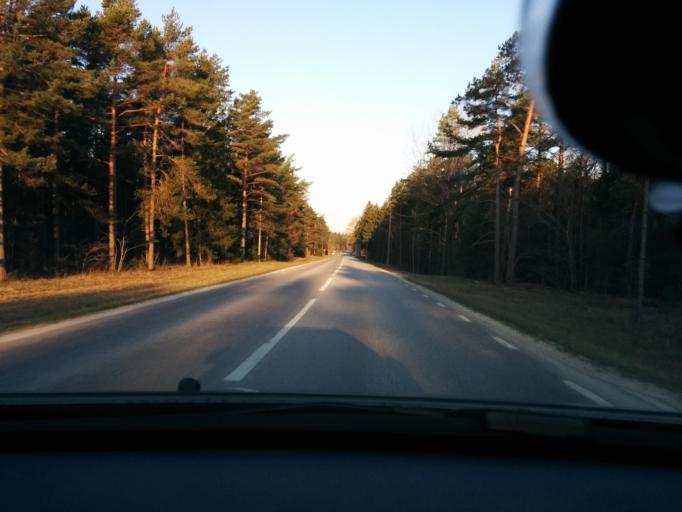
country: SE
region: Gotland
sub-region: Gotland
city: Visby
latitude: 57.6343
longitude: 18.5471
